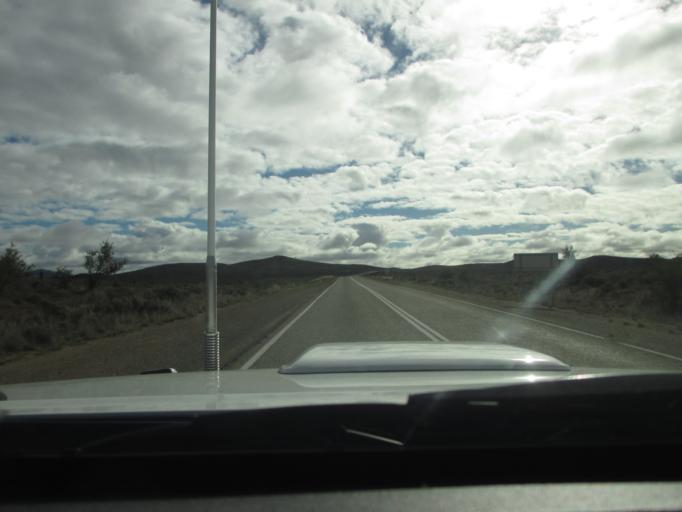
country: AU
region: South Australia
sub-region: Flinders Ranges
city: Quorn
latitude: -32.2791
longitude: 138.4951
